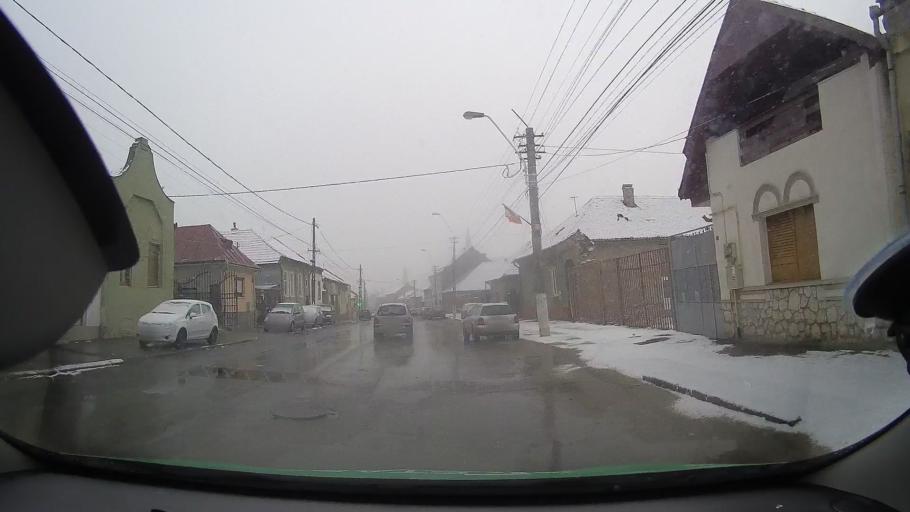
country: RO
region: Alba
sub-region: Municipiul Aiud
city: Aiud
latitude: 46.3104
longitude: 23.7132
